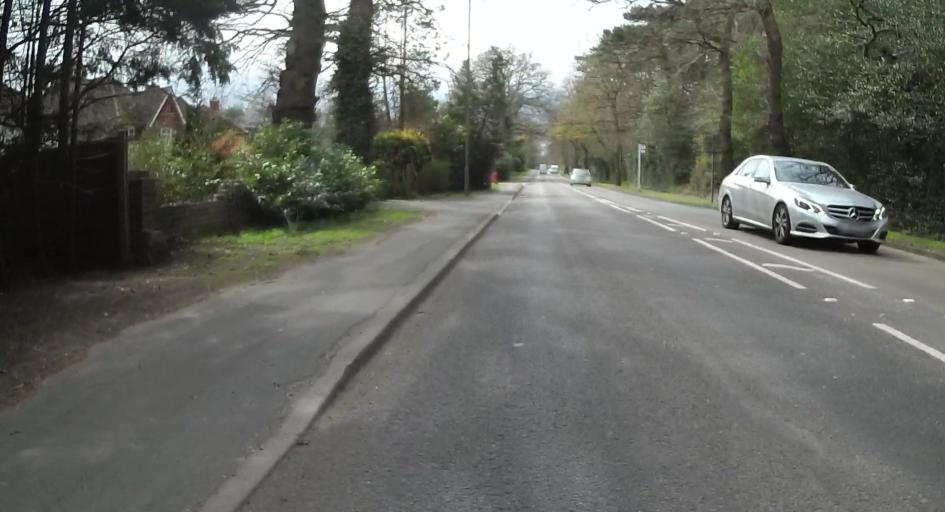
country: GB
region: England
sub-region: Surrey
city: Ottershaw
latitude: 51.3368
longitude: -0.5352
